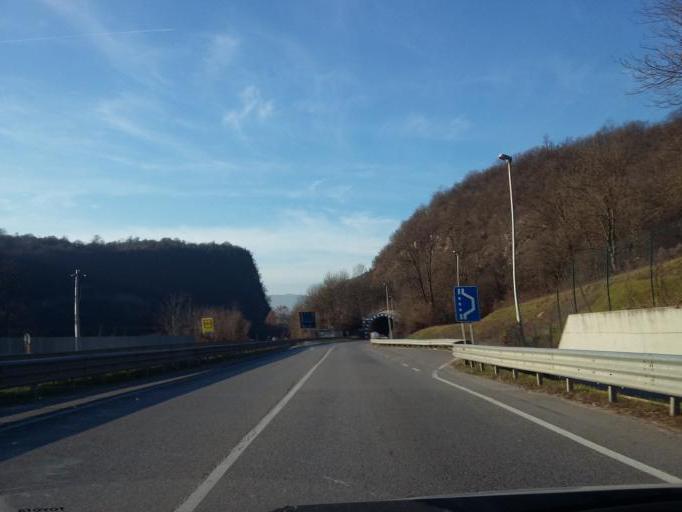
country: IT
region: Lombardy
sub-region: Provincia di Brescia
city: Sabbio Chiese
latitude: 45.6467
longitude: 10.4533
